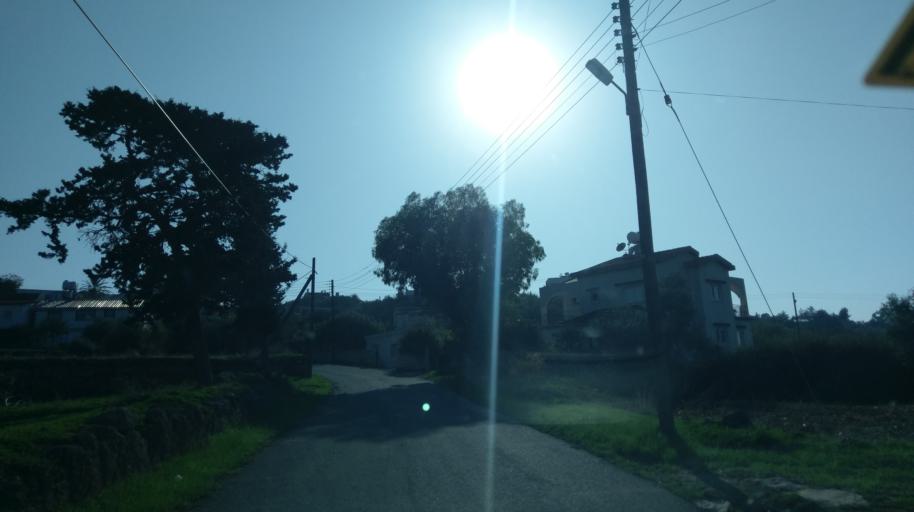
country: CY
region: Ammochostos
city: Leonarisso
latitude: 35.5389
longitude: 34.1911
